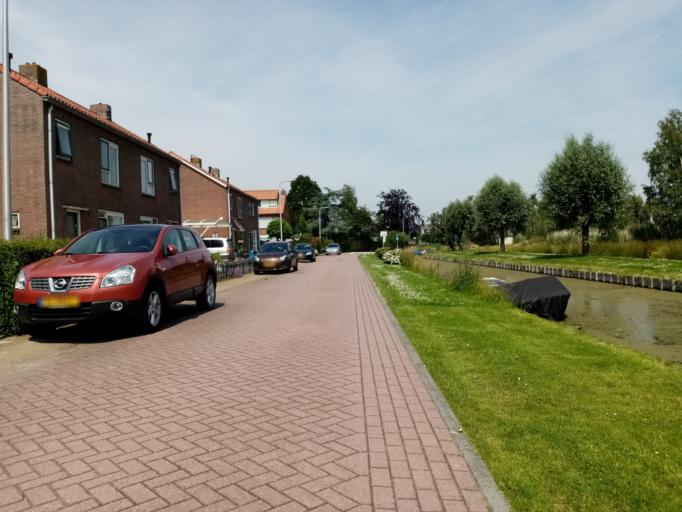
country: NL
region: South Holland
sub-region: Gemeente Nieuwkoop
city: Nieuwkoop
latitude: 52.1851
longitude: 4.7245
